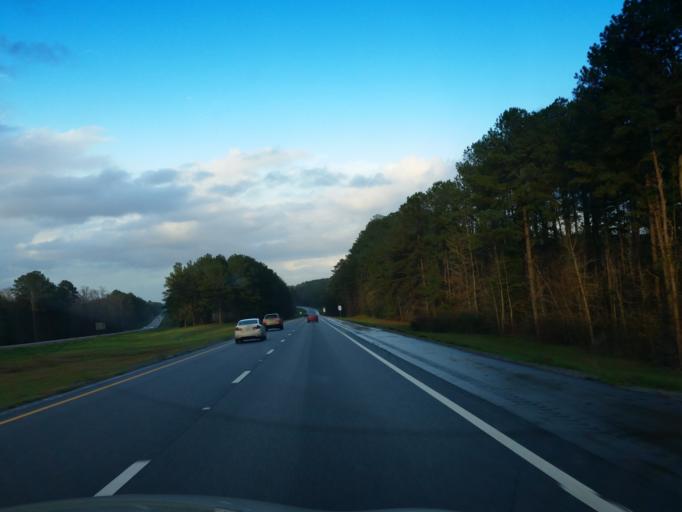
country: US
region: Mississippi
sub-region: Jones County
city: Sharon
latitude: 31.9684
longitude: -88.9630
